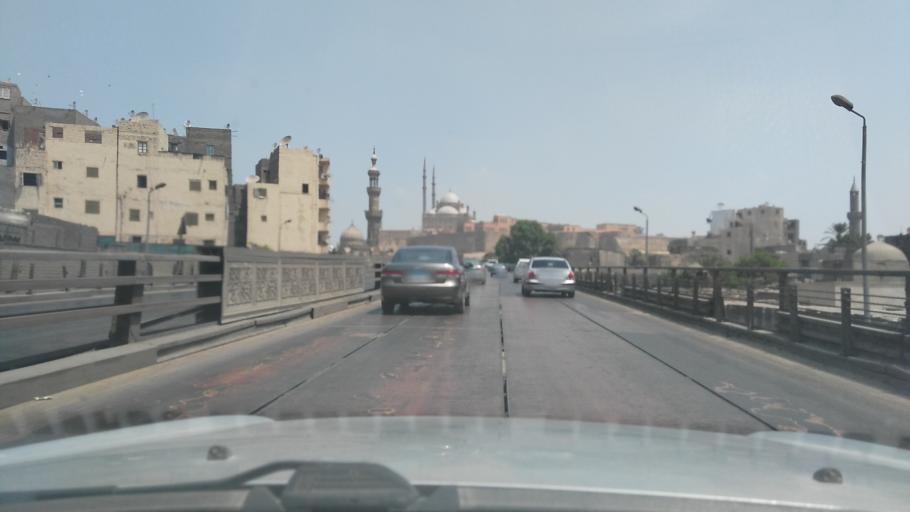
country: EG
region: Muhafazat al Qahirah
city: Cairo
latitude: 30.0232
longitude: 31.2560
